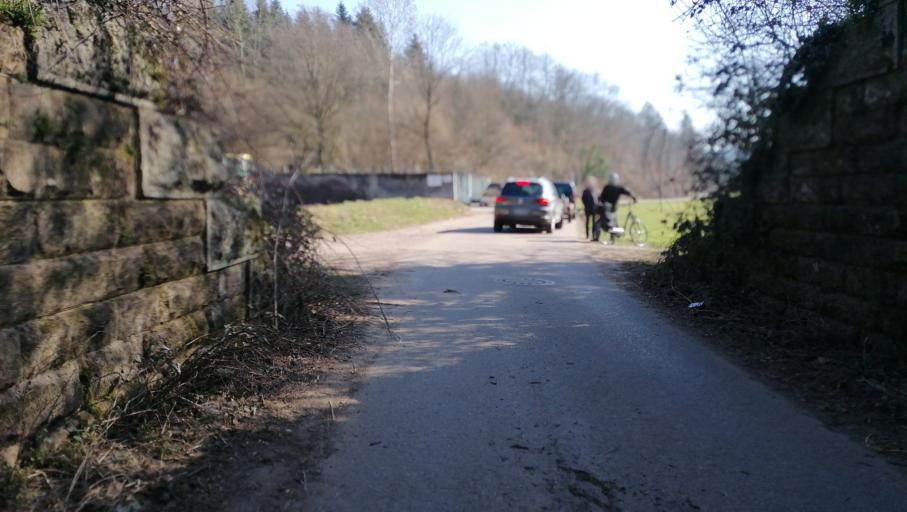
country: CH
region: Aargau
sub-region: Bezirk Rheinfelden
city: Mumpf
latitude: 47.5700
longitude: 7.9217
